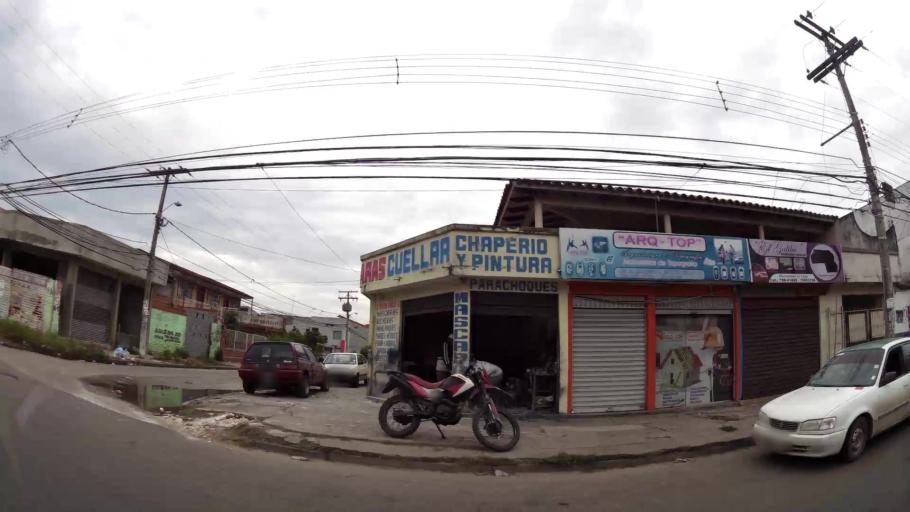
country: BO
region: Santa Cruz
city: Santa Cruz de la Sierra
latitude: -17.7689
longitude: -63.1648
